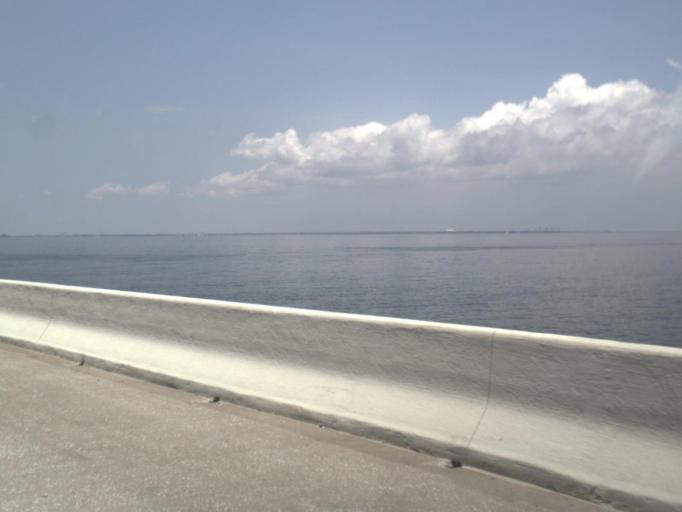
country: US
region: Florida
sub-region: Manatee County
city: Memphis
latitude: 27.5950
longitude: -82.6334
